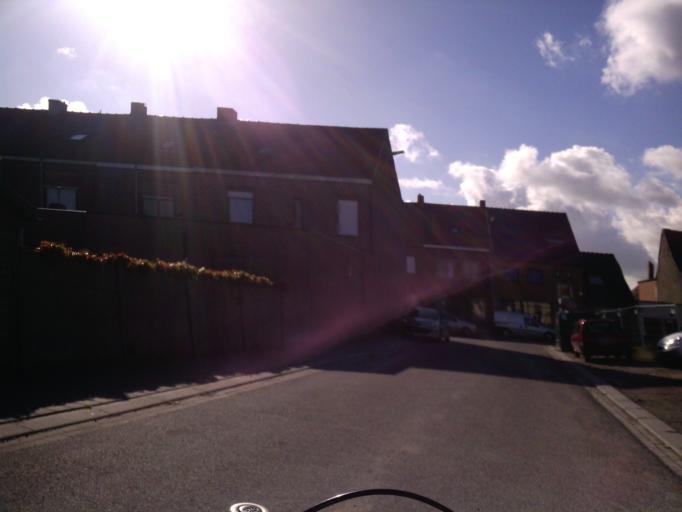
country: BE
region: Flanders
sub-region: Provincie West-Vlaanderen
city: Wevelgem
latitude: 50.7734
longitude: 3.1708
